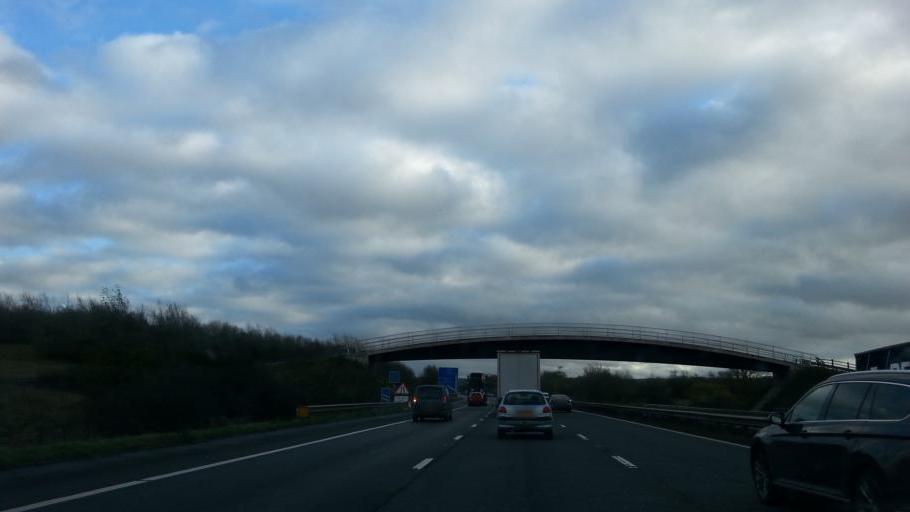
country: GB
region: England
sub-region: Wiltshire
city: Lydiard Tregoze
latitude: 51.5494
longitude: -1.8639
